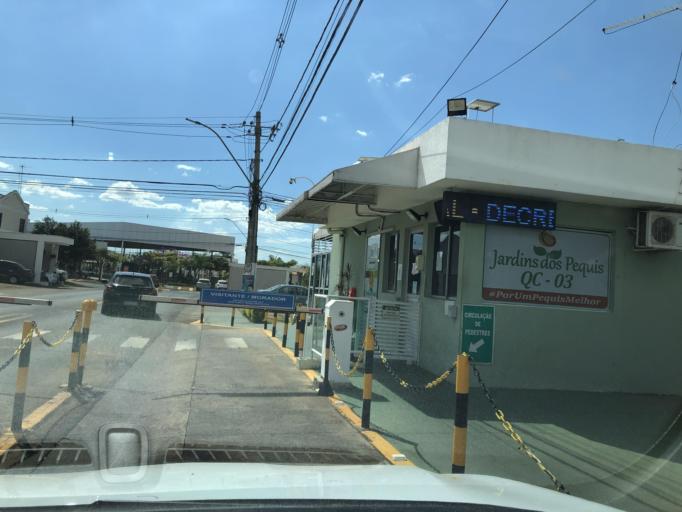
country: BR
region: Federal District
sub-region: Brasilia
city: Brasilia
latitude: -15.8886
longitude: -47.8150
